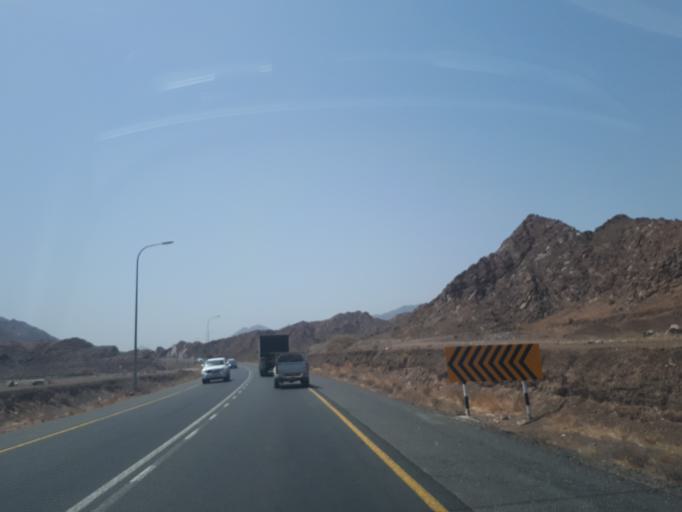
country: OM
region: Muhafazat ad Dakhiliyah
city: Sufalat Sama'il
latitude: 23.2133
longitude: 58.0771
